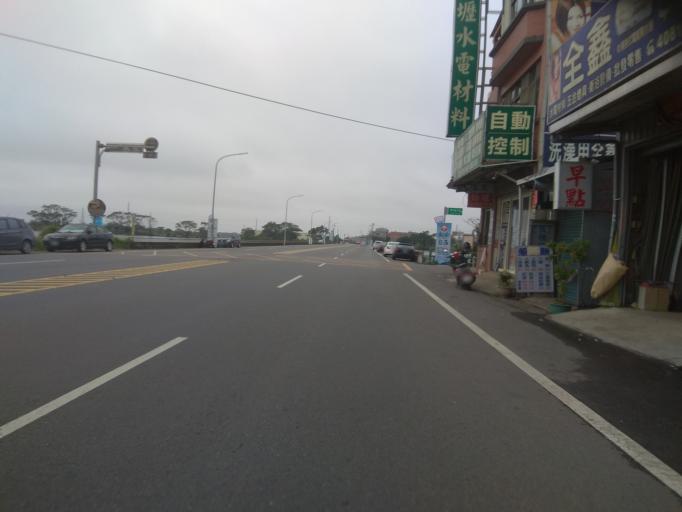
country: TW
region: Taiwan
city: Taoyuan City
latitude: 25.0112
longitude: 121.1362
